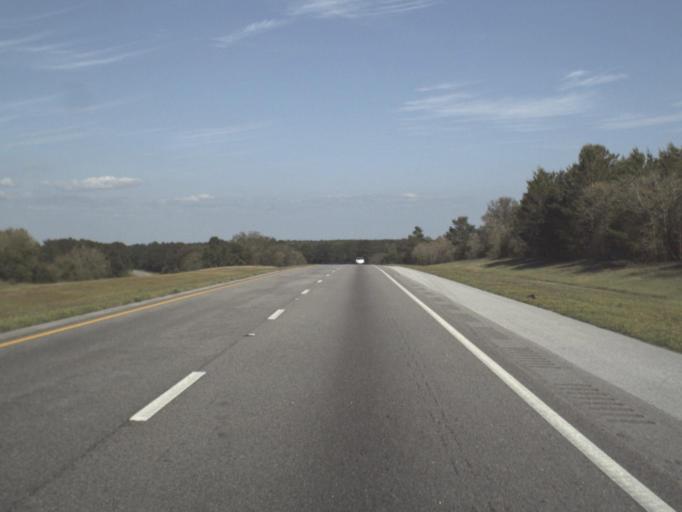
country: US
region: Florida
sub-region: Okaloosa County
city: Crestview
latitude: 30.7176
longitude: -86.4488
